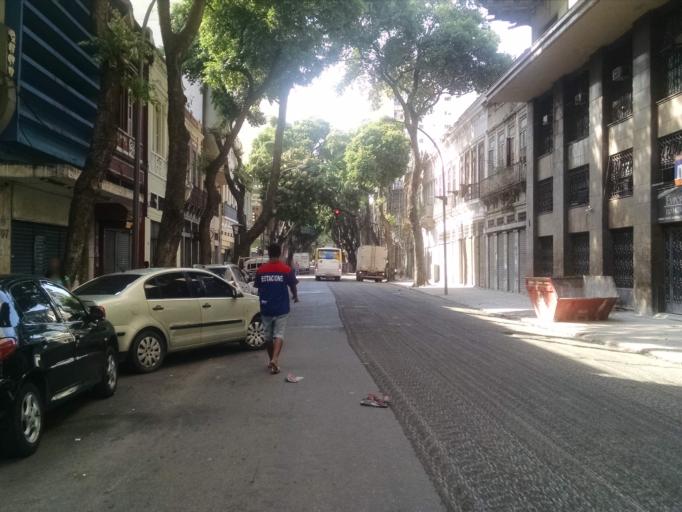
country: BR
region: Rio de Janeiro
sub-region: Rio De Janeiro
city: Rio de Janeiro
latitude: -22.9085
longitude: -43.1848
